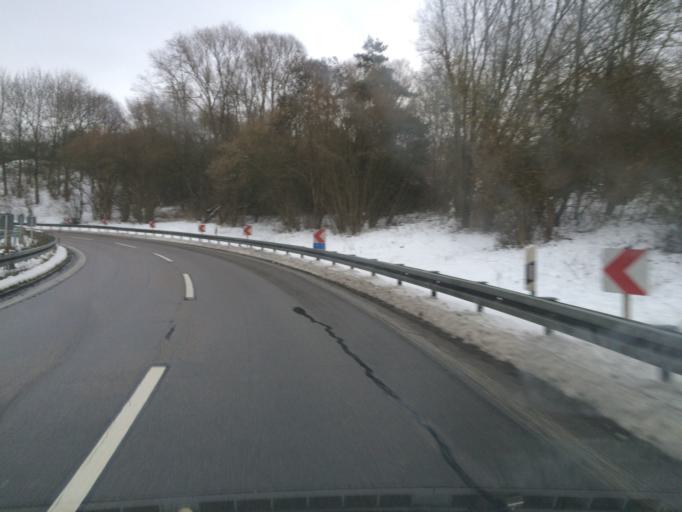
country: DE
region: Bavaria
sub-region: Upper Palatinate
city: Pentling
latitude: 49.0012
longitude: 12.0613
